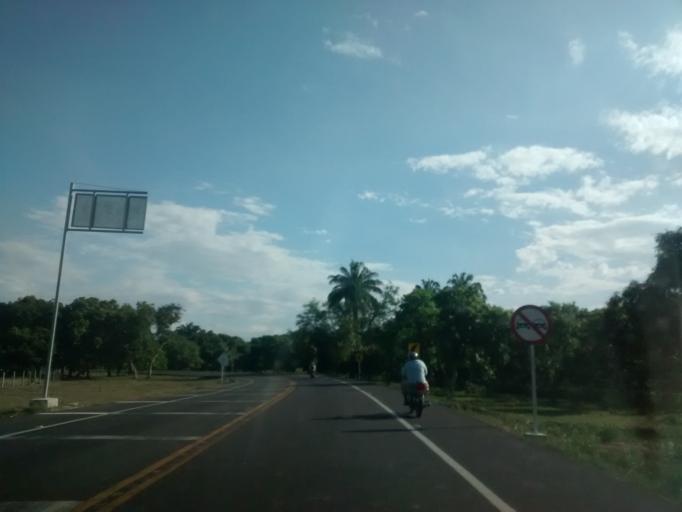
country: CO
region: Tolima
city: Espinal
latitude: 4.1644
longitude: -74.9183
